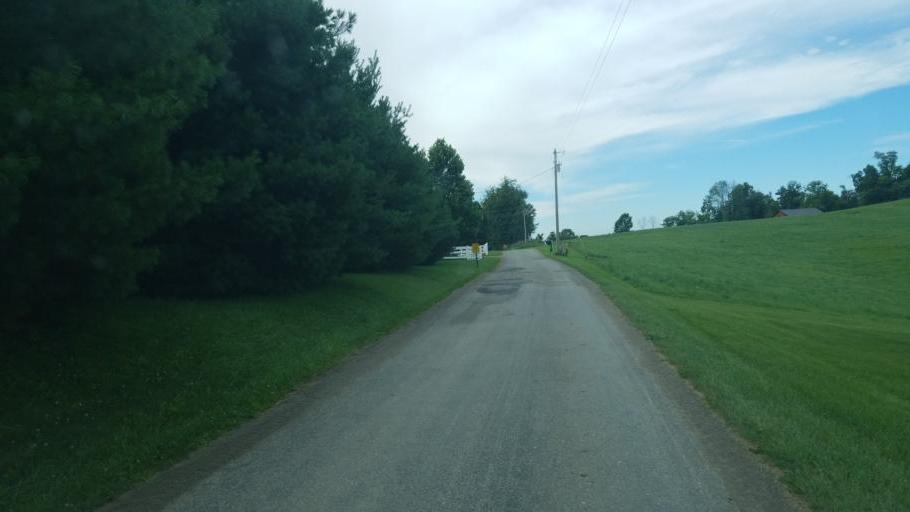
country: US
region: Ohio
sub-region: Holmes County
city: Millersburg
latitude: 40.5014
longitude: -81.8487
